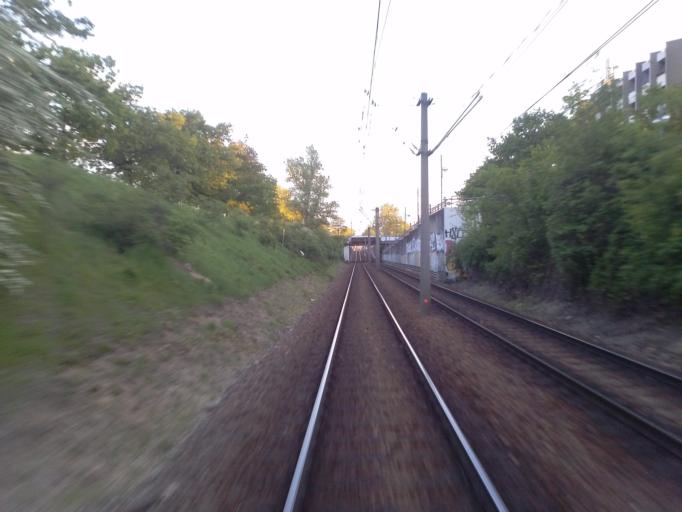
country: DE
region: Baden-Wuerttemberg
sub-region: Karlsruhe Region
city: Karlsruhe
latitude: 49.0229
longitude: 8.3757
